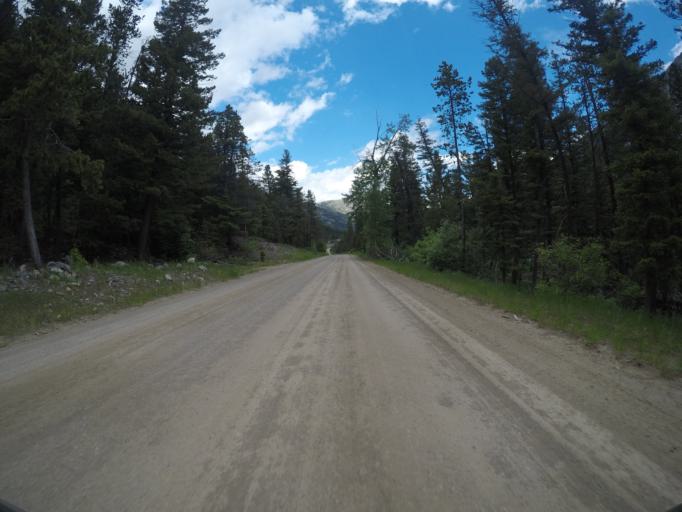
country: US
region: Montana
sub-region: Park County
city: Livingston
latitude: 45.4972
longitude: -110.2262
